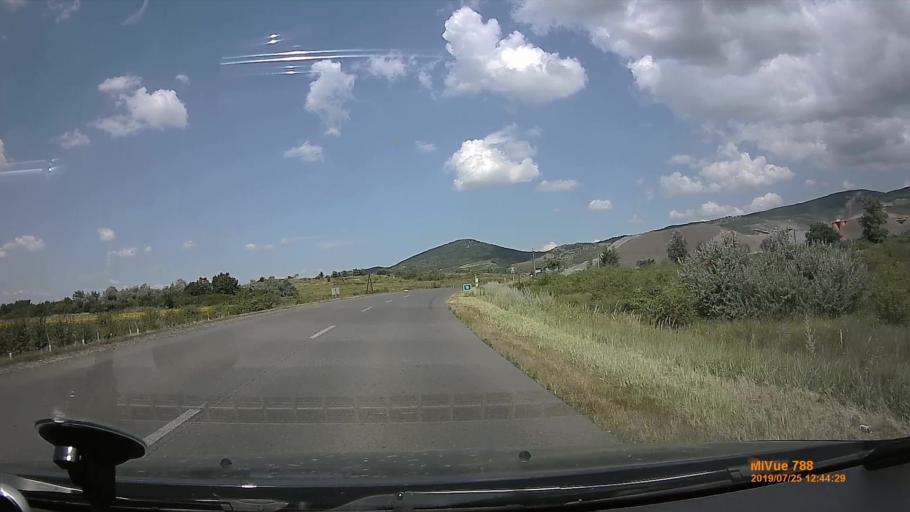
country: HU
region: Borsod-Abauj-Zemplen
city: Tallya
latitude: 48.2342
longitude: 21.2128
